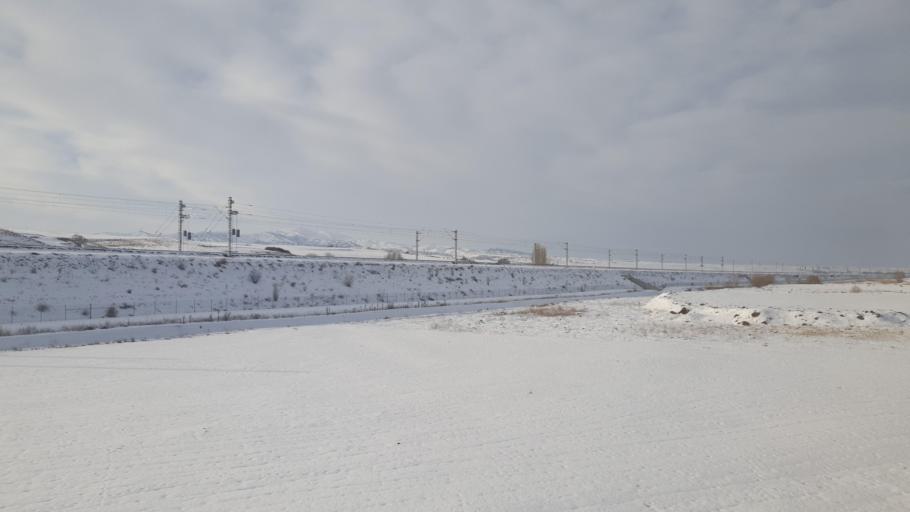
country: TR
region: Kirikkale
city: Baliseyh
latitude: 39.9270
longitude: 33.7853
